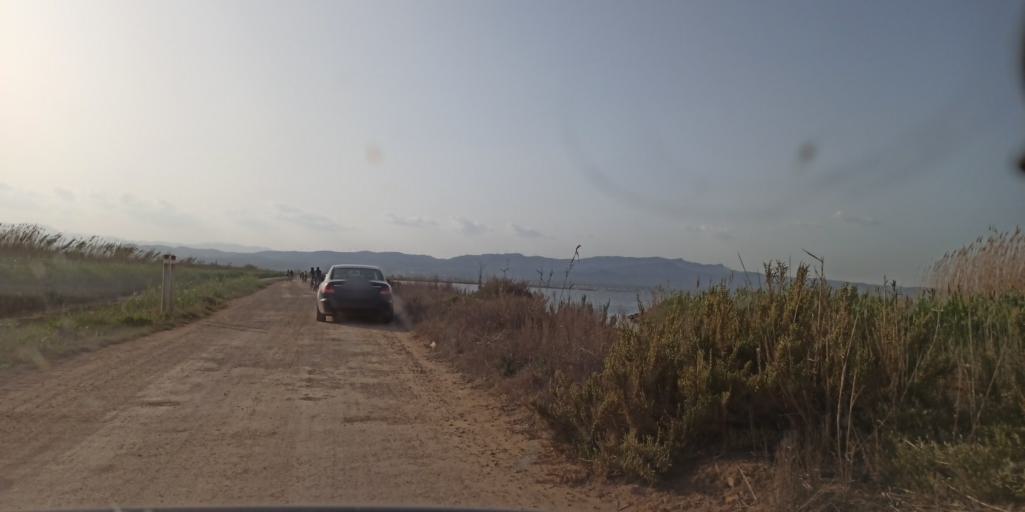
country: ES
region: Catalonia
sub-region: Provincia de Tarragona
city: L'Ampolla
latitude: 40.7672
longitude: 0.7360
